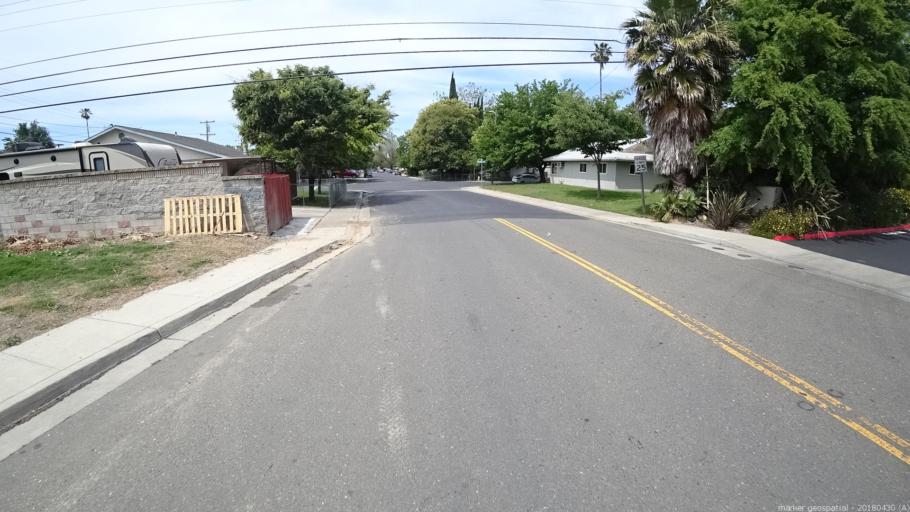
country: US
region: California
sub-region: Yolo County
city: West Sacramento
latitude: 38.5567
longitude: -121.5338
